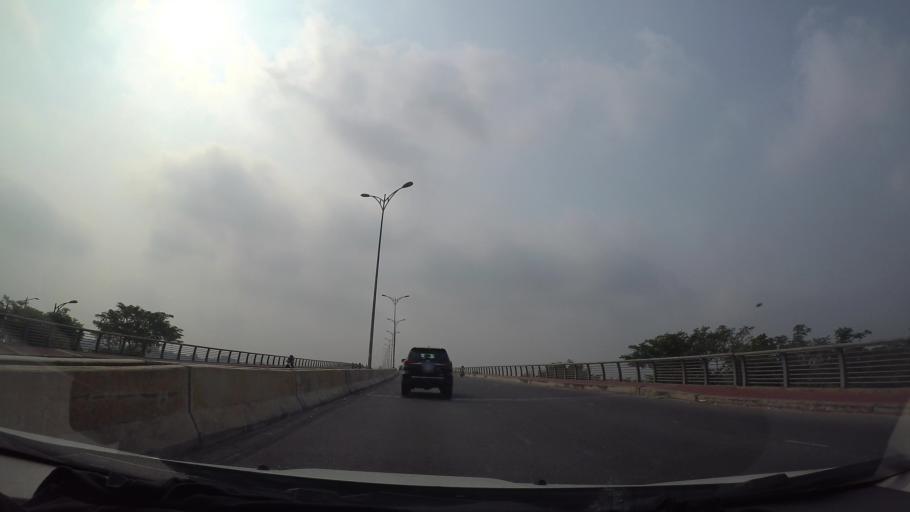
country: VN
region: Da Nang
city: Cam Le
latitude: 16.0181
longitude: 108.2122
